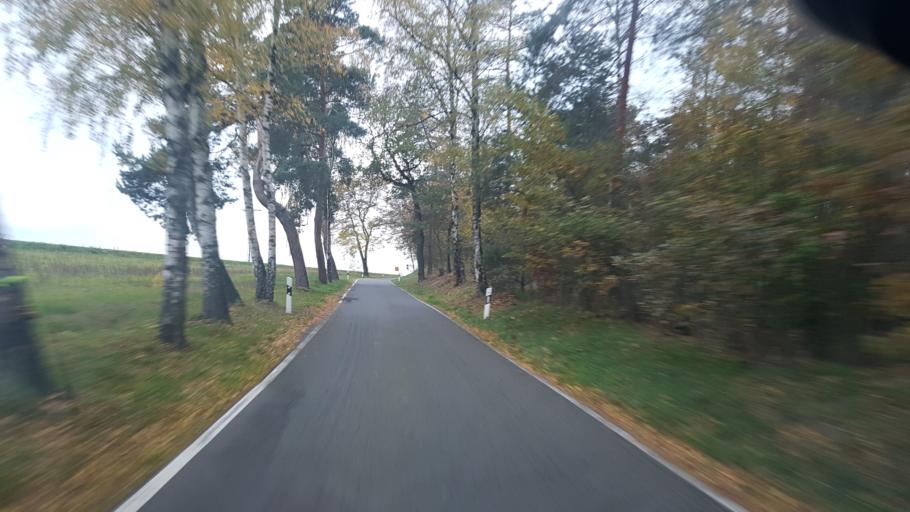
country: DE
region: Saxony
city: Cavertitz
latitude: 51.3898
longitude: 13.0714
